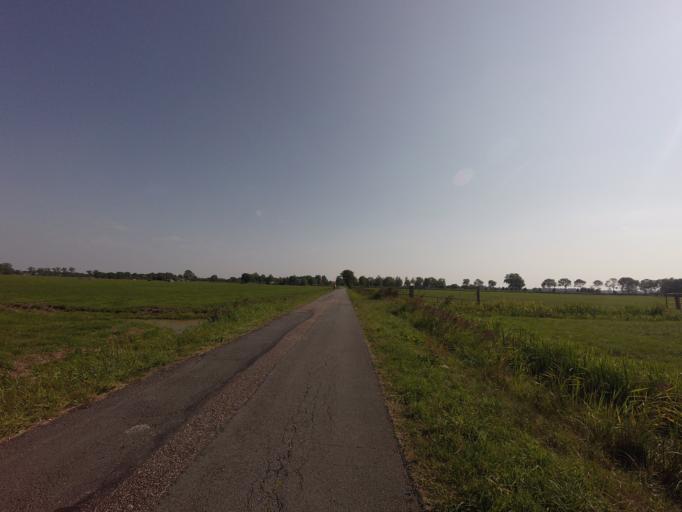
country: NL
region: Groningen
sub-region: Gemeente Zuidhorn
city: Zuidhorn
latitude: 53.2139
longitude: 6.4327
